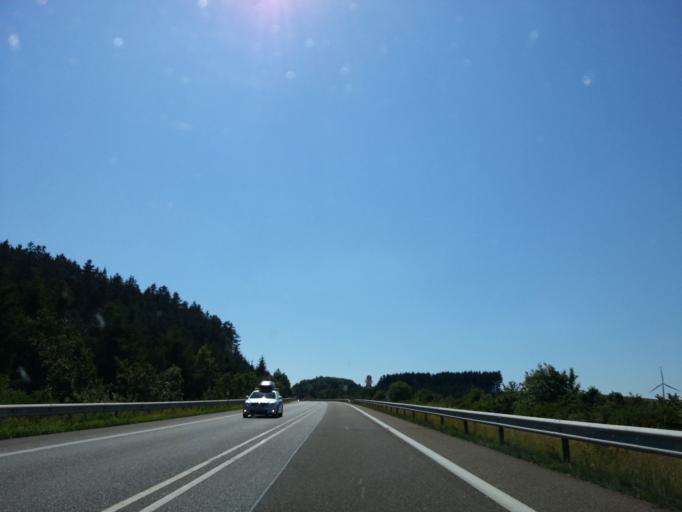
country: DE
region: Rheinland-Pfalz
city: Grosslangenfeld
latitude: 50.2068
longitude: 6.2462
